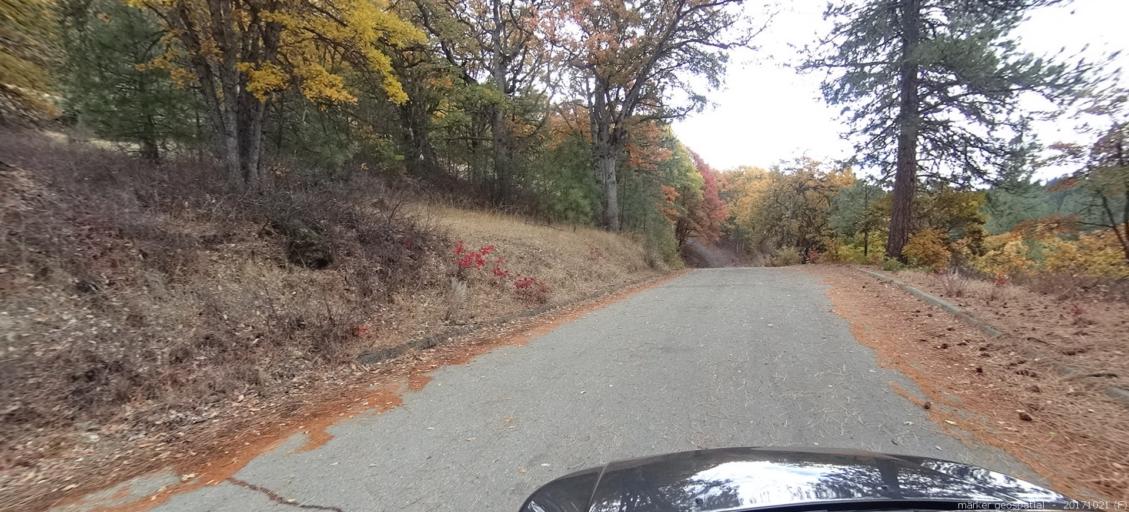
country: US
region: California
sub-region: Shasta County
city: Burney
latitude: 41.0229
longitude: -121.6235
